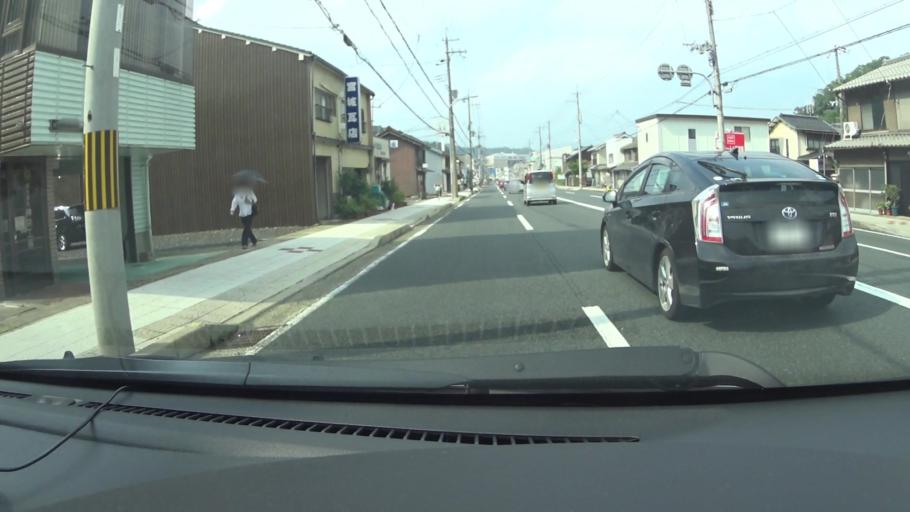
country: JP
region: Kyoto
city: Maizuru
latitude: 35.4705
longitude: 135.3655
